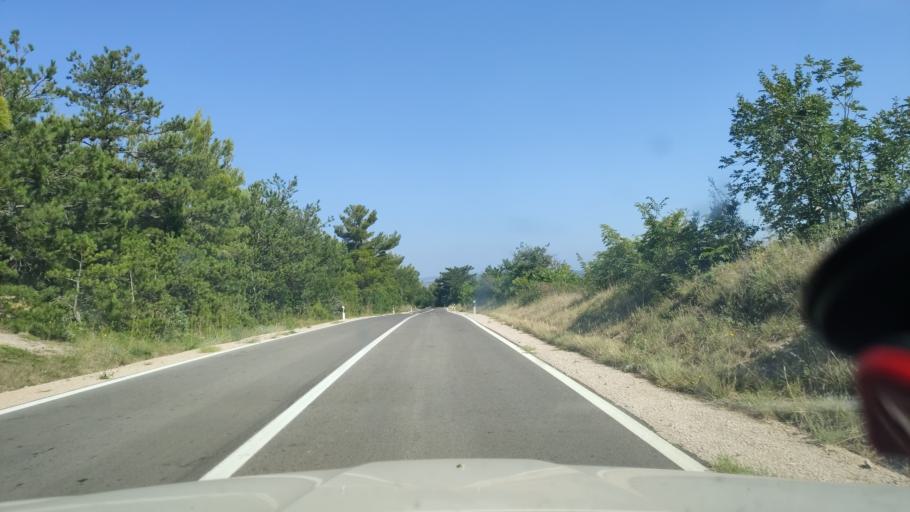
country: HR
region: Sibensko-Kniniska
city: Zaton
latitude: 43.9179
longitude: 15.8253
